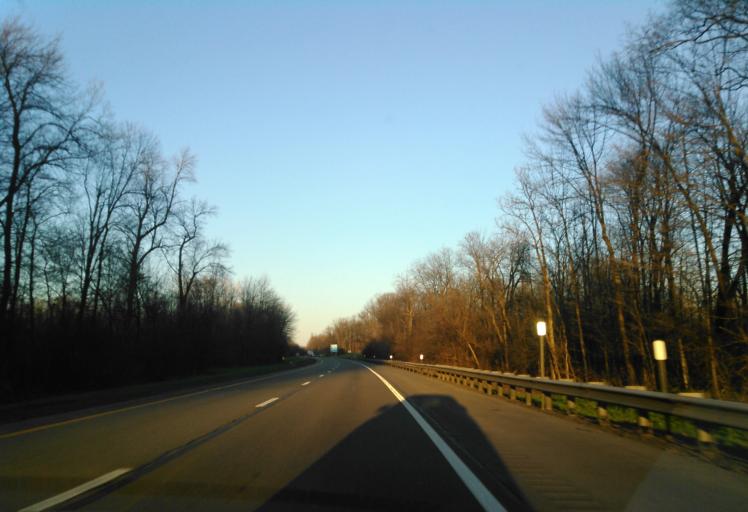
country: US
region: New York
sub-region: Ontario County
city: Shortsville
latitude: 42.9749
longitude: -77.2040
